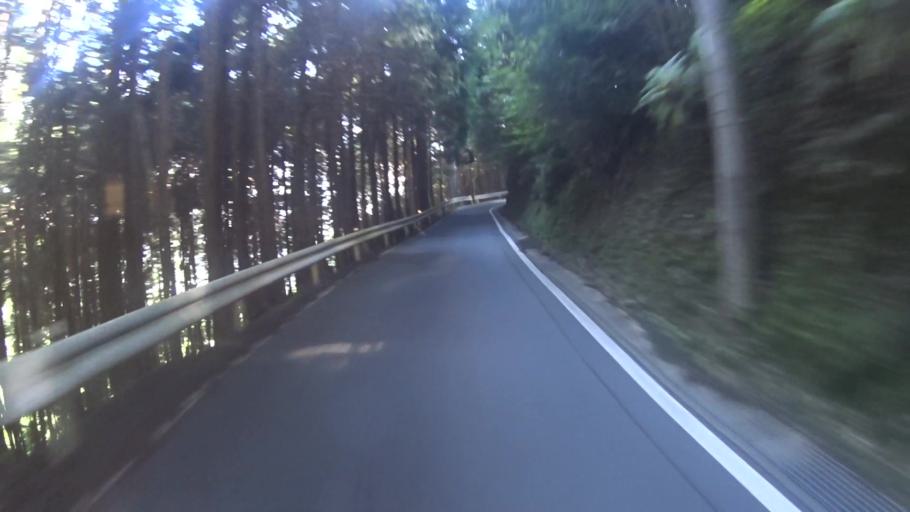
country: JP
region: Kyoto
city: Uji
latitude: 34.8083
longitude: 135.8944
